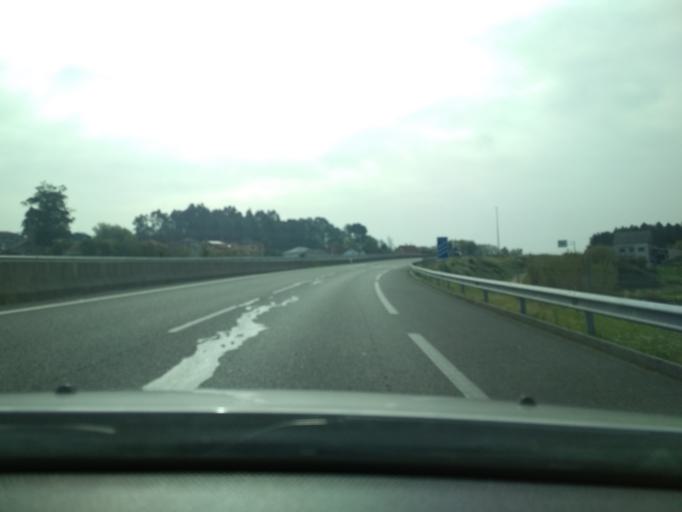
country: ES
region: Galicia
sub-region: Provincia da Coruna
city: Rianxo
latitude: 42.6735
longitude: -8.8316
